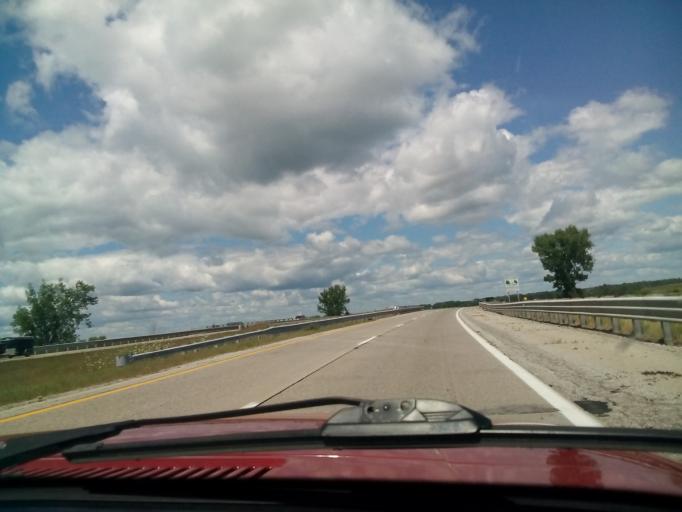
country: US
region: Michigan
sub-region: Bay County
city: Auburn
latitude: 43.6665
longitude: -84.0113
